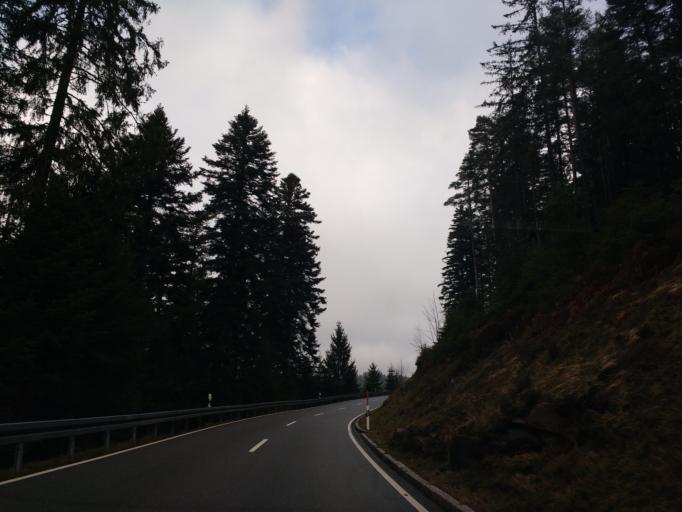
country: DE
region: Baden-Wuerttemberg
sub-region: Karlsruhe Region
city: Bad Rippoldsau-Schapbach
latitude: 48.4544
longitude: 8.2926
